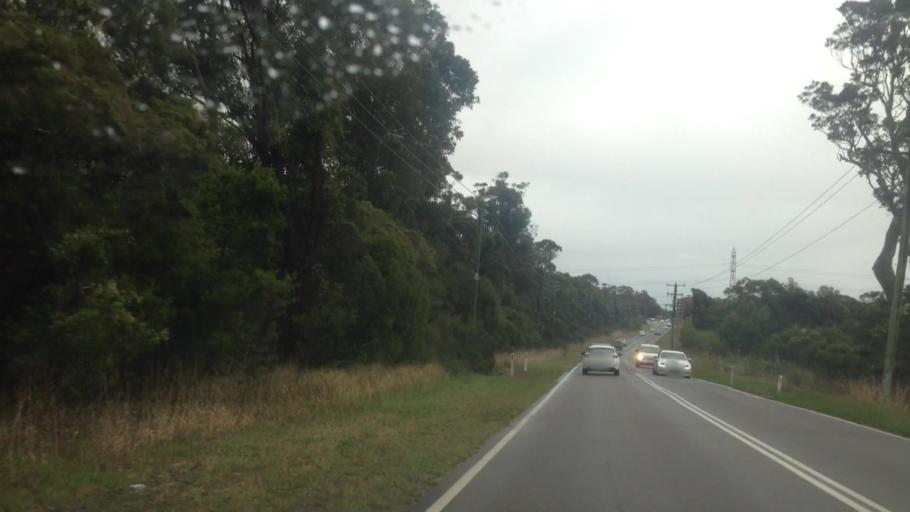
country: AU
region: New South Wales
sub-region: Wyong Shire
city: Charmhaven
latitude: -33.1622
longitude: 151.4784
